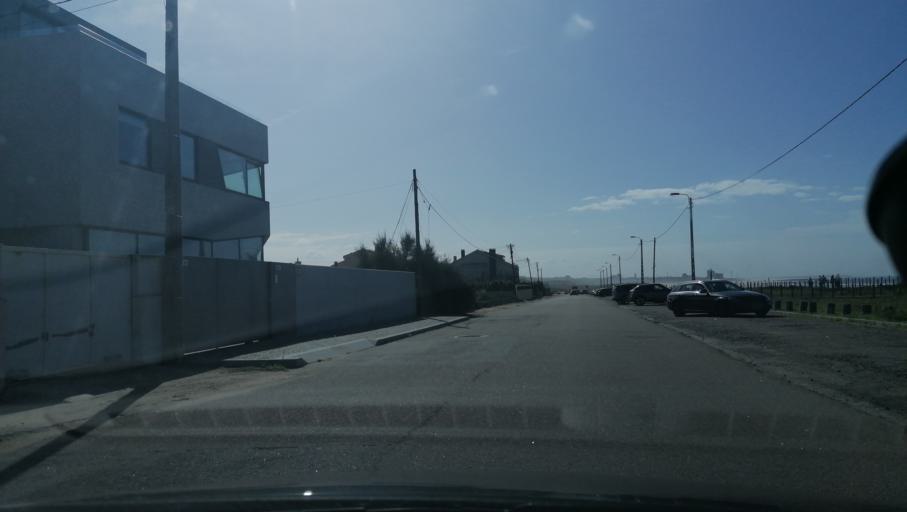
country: PT
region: Porto
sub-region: Vila Nova de Gaia
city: Arcozelo
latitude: 41.0360
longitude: -8.6474
